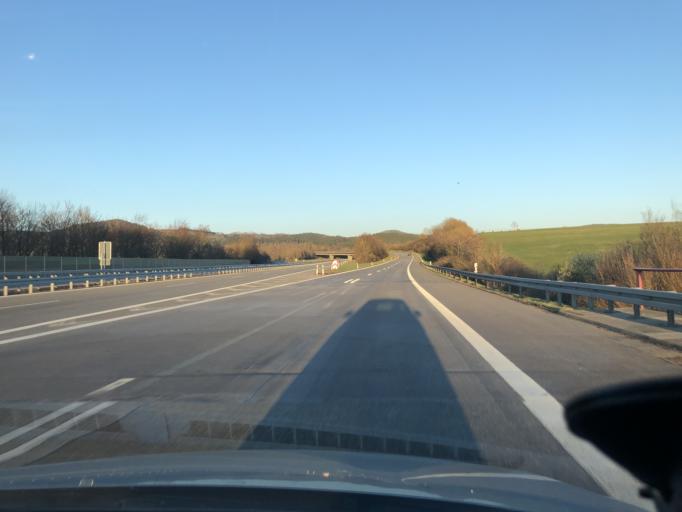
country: DE
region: Baden-Wuerttemberg
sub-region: Freiburg Region
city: Tuningen
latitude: 47.9941
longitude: 8.5933
